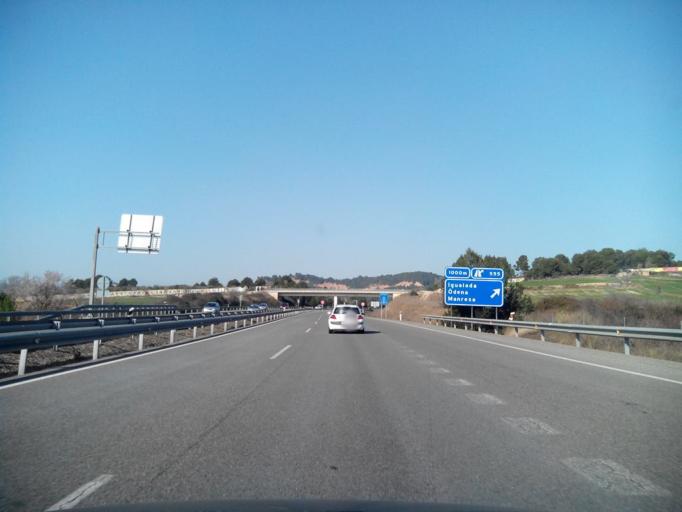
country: ES
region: Catalonia
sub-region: Provincia de Barcelona
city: Odena
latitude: 41.5947
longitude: 1.6468
